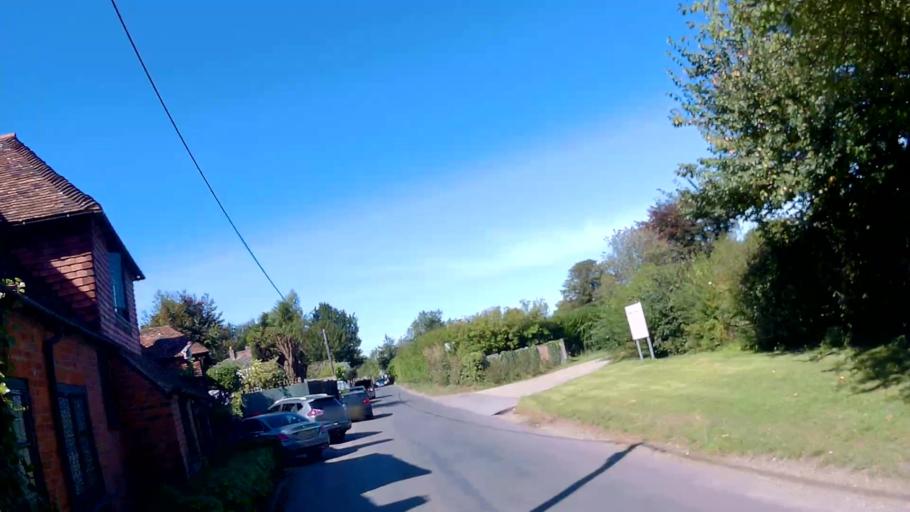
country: GB
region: England
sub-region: Hampshire
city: Overton
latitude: 51.2494
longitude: -1.1868
